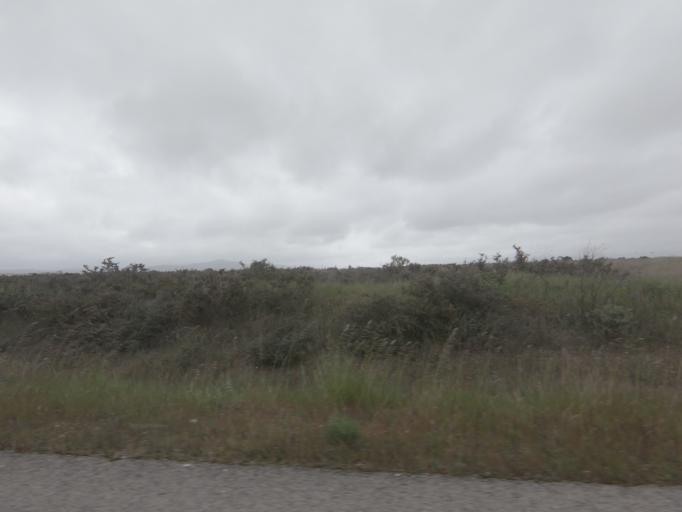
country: ES
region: Extremadura
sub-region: Provincia de Caceres
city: Malpartida de Caceres
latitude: 39.3390
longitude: -6.4792
